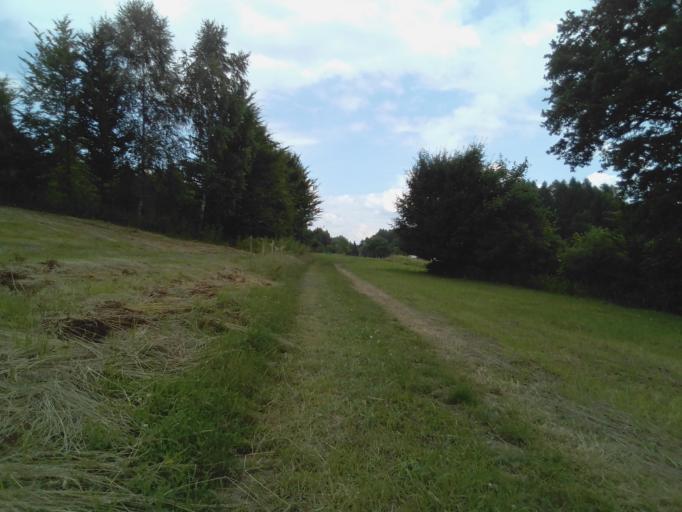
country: PL
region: Subcarpathian Voivodeship
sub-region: Powiat strzyzowski
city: Strzyzow
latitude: 49.8822
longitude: 21.7835
